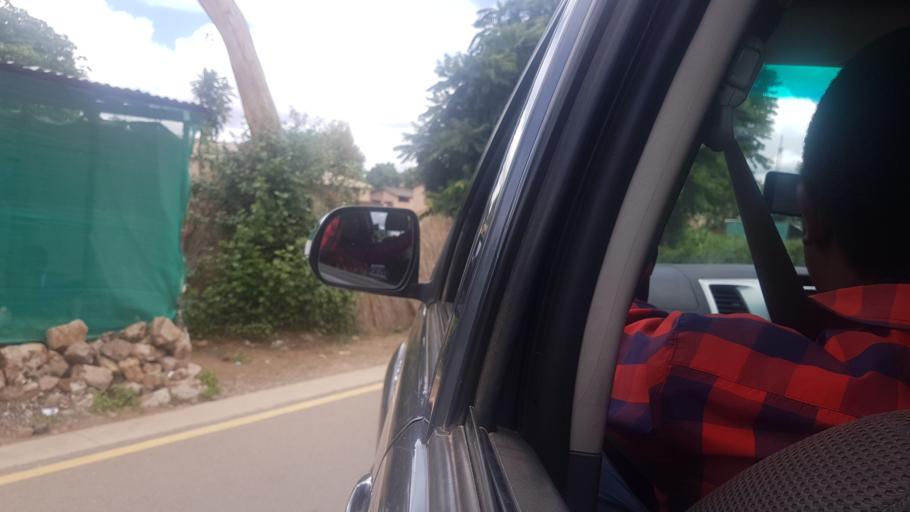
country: ZM
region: Lusaka
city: Lusaka
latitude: -15.4269
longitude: 28.3048
